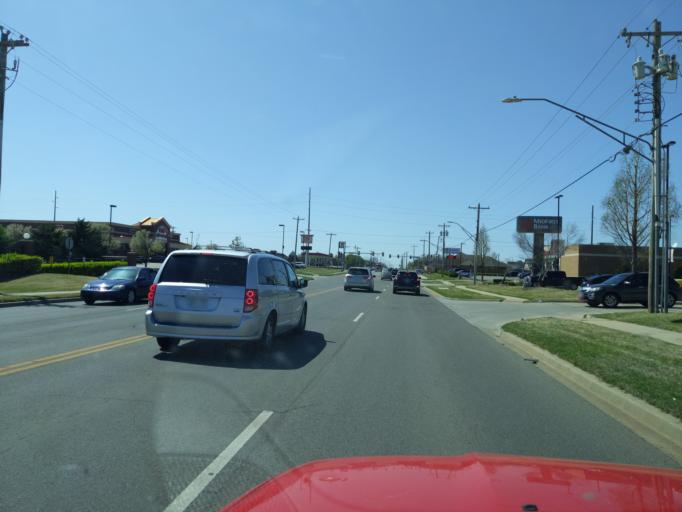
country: US
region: Oklahoma
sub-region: Cleveland County
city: Moore
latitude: 35.3199
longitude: -97.5100
